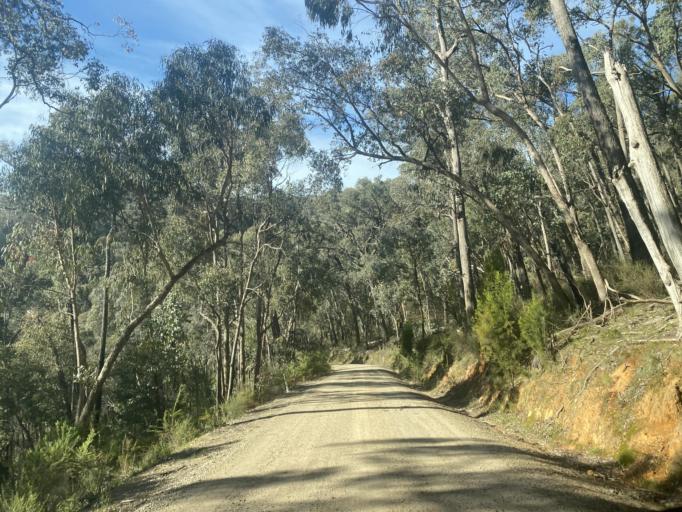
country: AU
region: Victoria
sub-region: Mansfield
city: Mansfield
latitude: -36.8311
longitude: 146.1644
